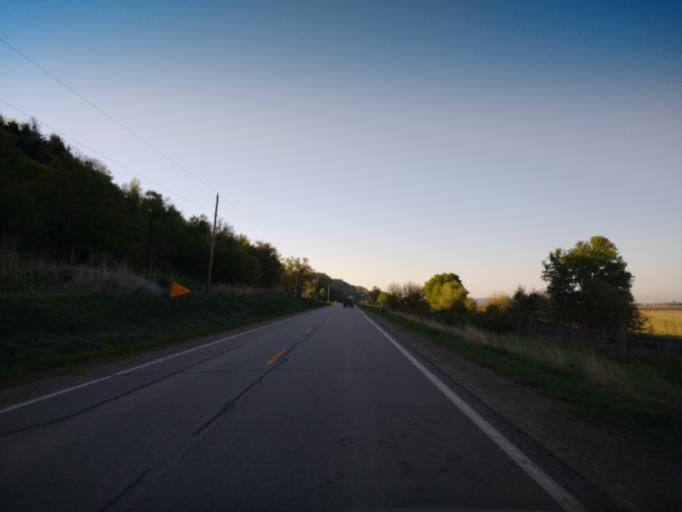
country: US
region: Iowa
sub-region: Harrison County
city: Missouri Valley
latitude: 41.4870
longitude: -95.8870
